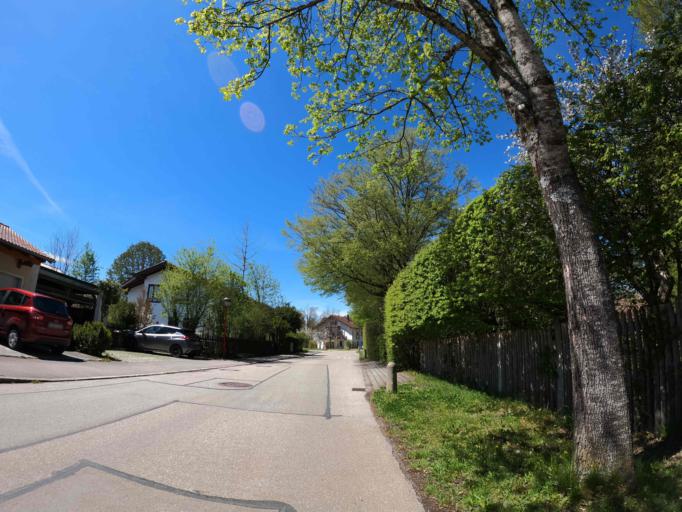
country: DE
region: Bavaria
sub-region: Upper Bavaria
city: Oberhaching
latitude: 48.0281
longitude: 11.5729
